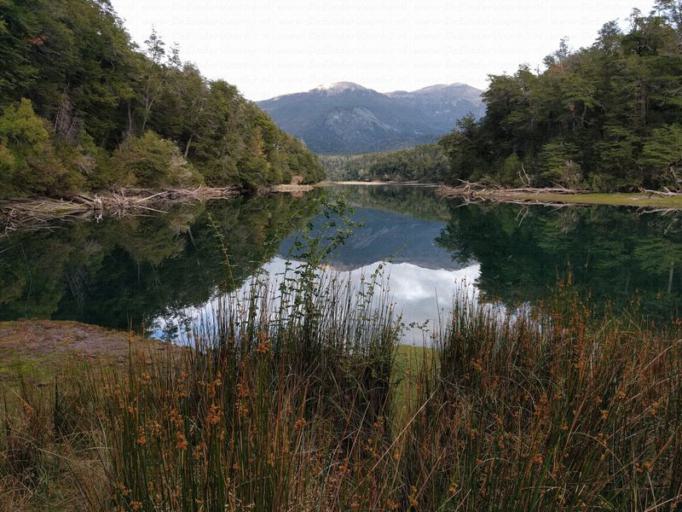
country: AR
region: Chubut
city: Trevelin
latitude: -42.7448
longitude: -71.7433
